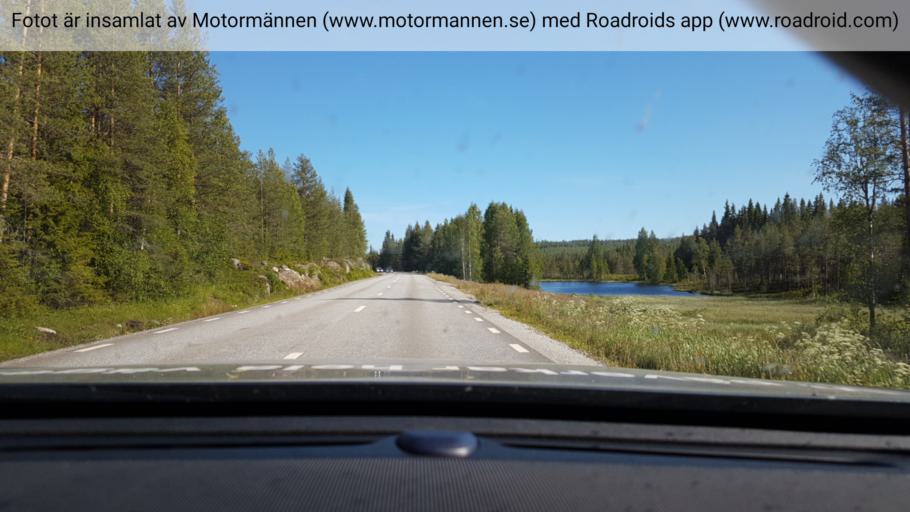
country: SE
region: Vaesterbotten
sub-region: Lycksele Kommun
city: Lycksele
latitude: 64.6840
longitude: 18.4145
